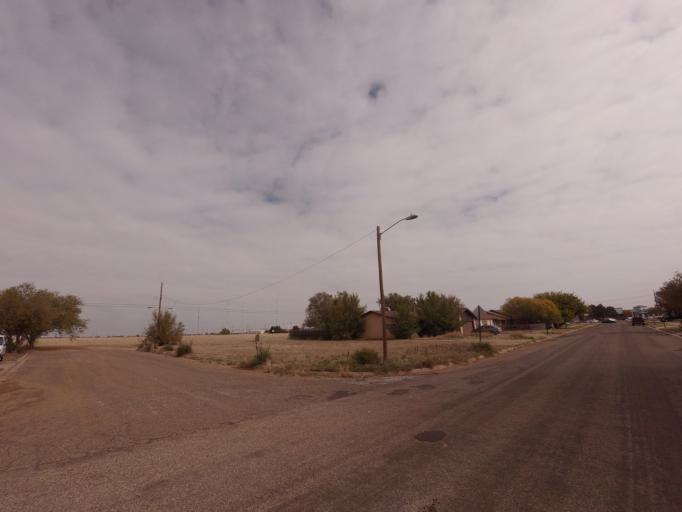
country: US
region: New Mexico
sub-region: Curry County
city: Clovis
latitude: 34.4313
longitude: -103.2159
